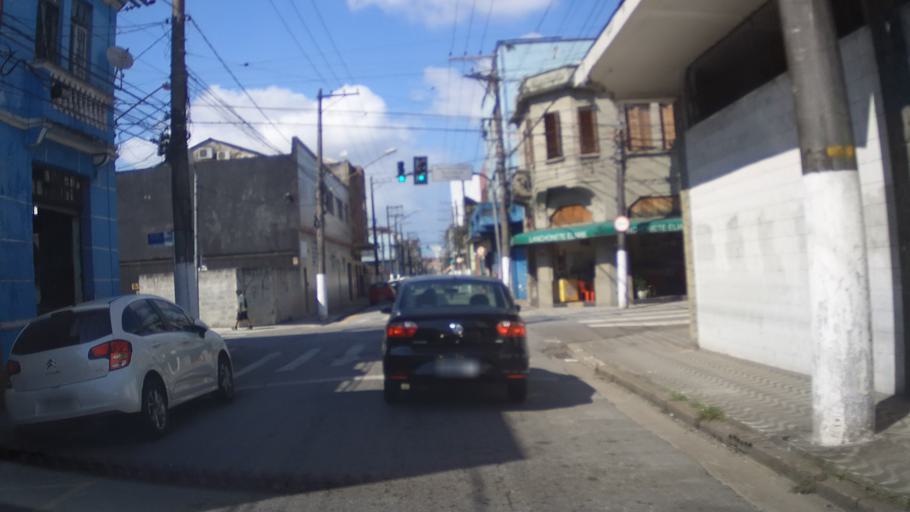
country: BR
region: Sao Paulo
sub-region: Santos
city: Santos
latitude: -23.9378
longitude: -46.3227
